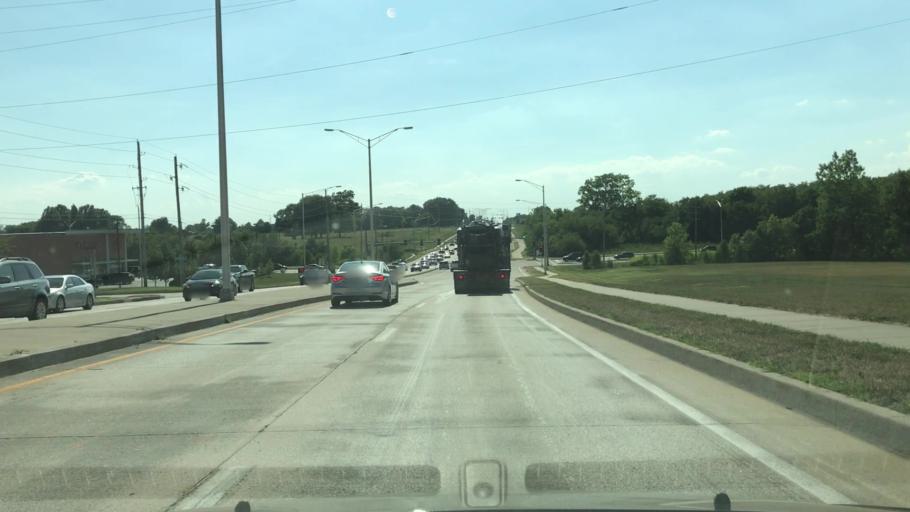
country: US
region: Missouri
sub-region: Cass County
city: Lake Winnebago
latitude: 38.8533
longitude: -94.3964
